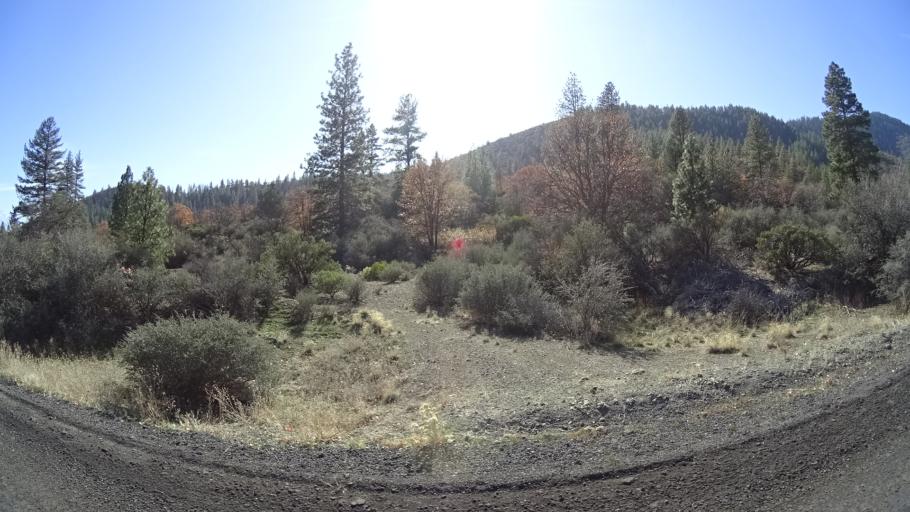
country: US
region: California
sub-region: Siskiyou County
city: Yreka
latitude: 41.7736
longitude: -122.6480
